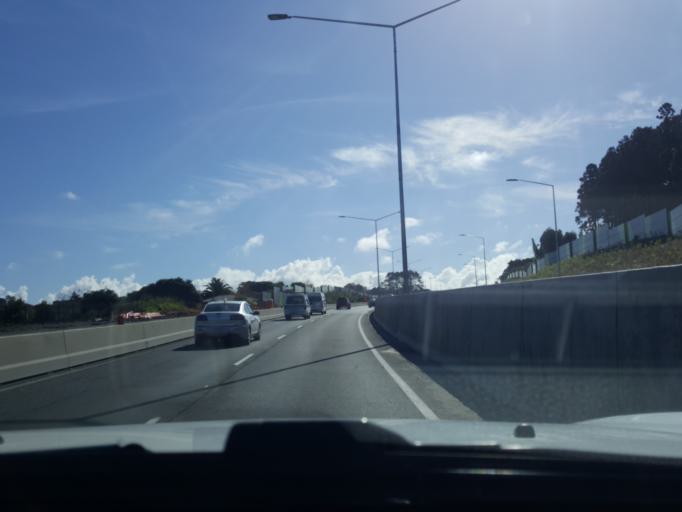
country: NZ
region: Auckland
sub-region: Auckland
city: Rosebank
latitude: -36.8389
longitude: 174.6206
